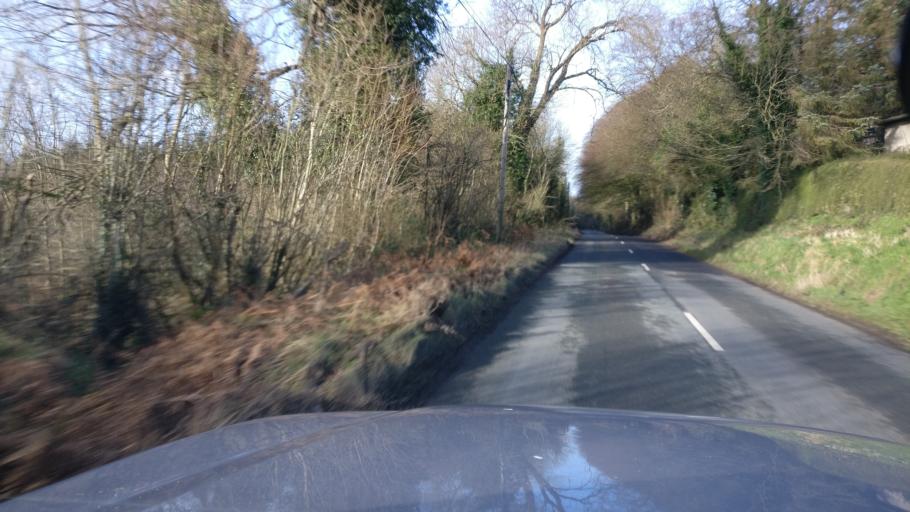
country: IE
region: Leinster
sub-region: Laois
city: Stradbally
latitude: 52.9415
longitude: -7.1992
